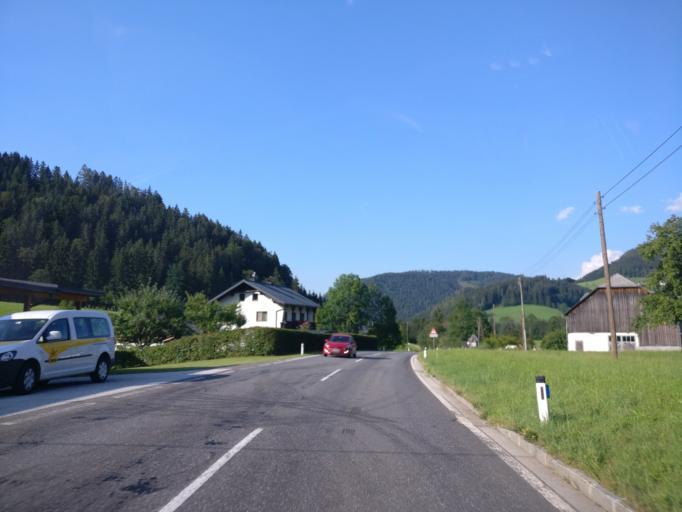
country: AT
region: Lower Austria
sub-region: Politischer Bezirk Scheibbs
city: Gostling an der Ybbs
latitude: 47.7535
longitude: 14.9007
